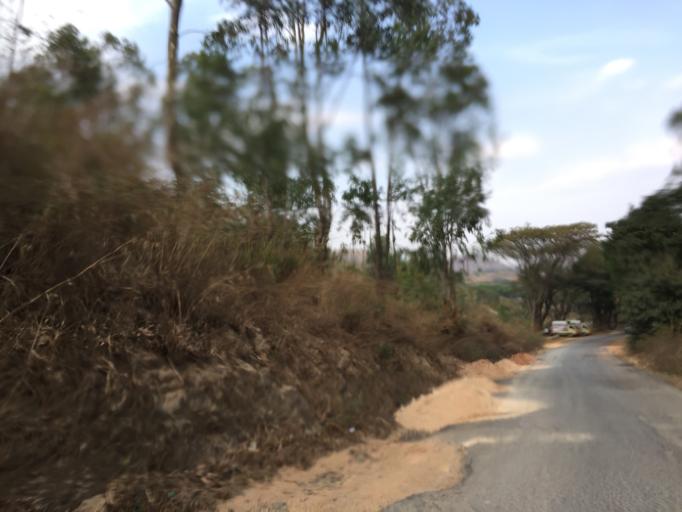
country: IN
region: Karnataka
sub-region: Chikkaballapur
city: Chik Ballapur
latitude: 13.3774
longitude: 77.6721
